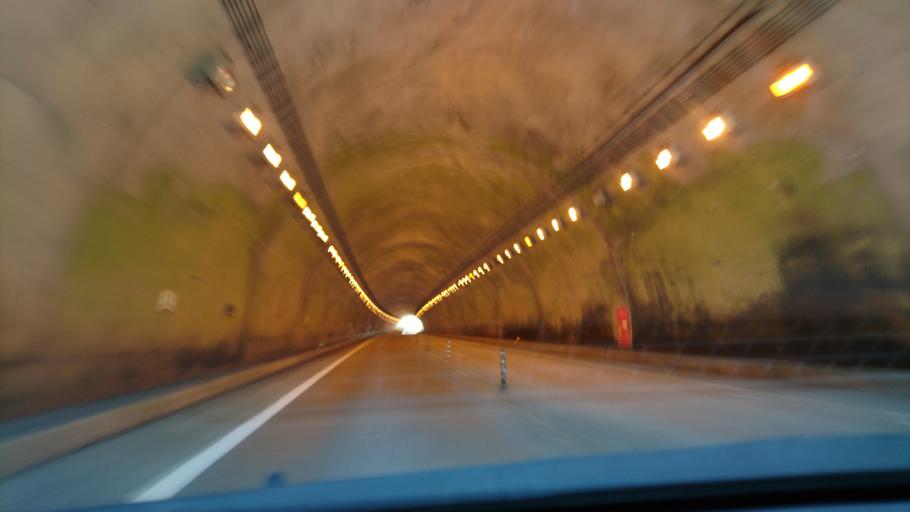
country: JP
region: Iwate
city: Ofunato
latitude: 39.0571
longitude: 141.7120
